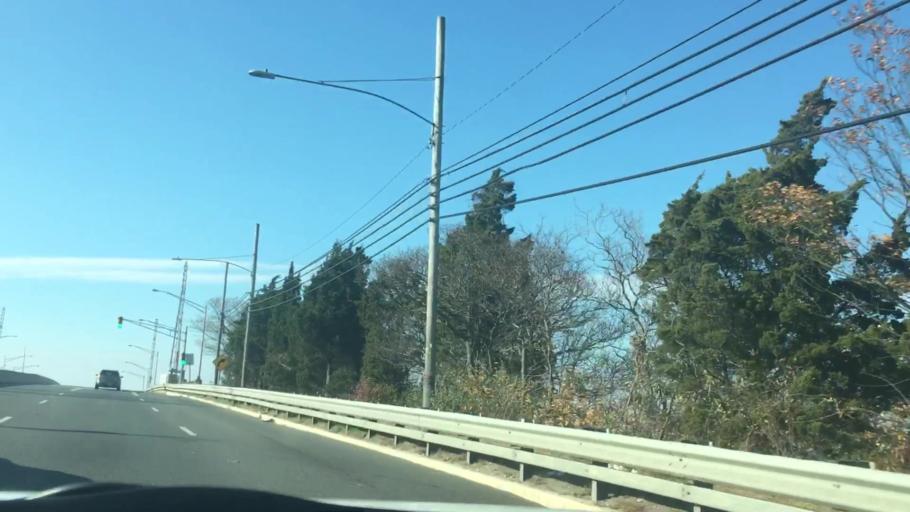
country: US
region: New Jersey
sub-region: Atlantic County
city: Atlantic City
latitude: 39.3770
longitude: -74.4508
